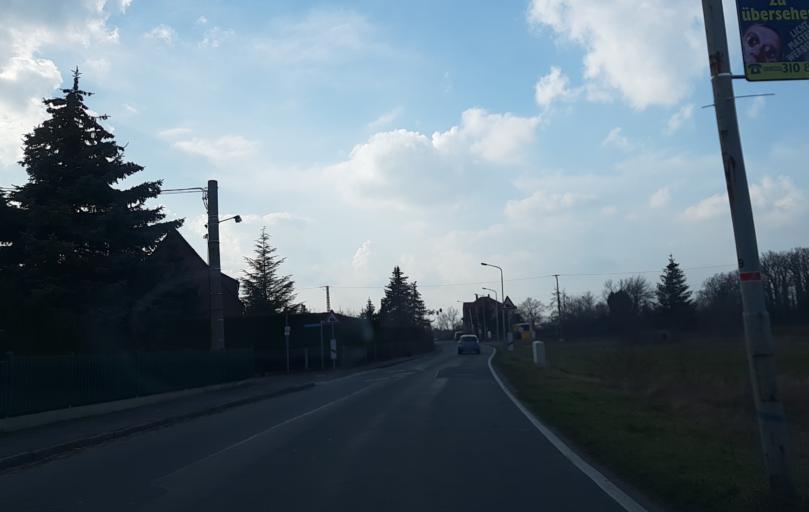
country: DE
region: Saxony
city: Grossenhain
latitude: 51.2847
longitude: 13.5178
